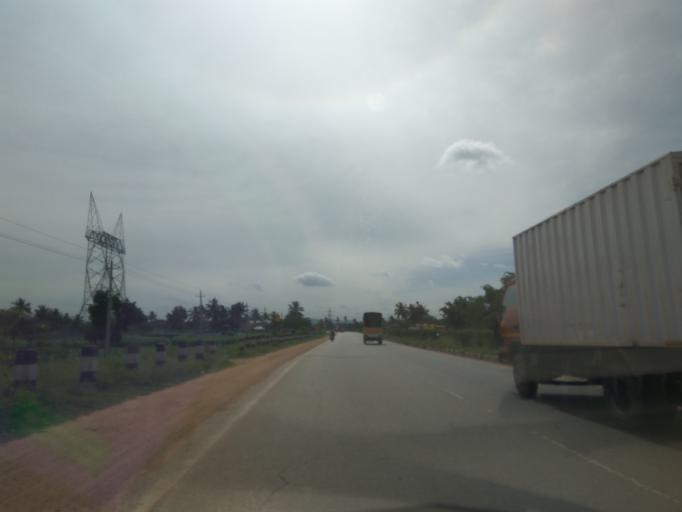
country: IN
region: Karnataka
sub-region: Bangalore Rural
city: Dasarahalli
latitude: 13.1345
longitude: 77.9394
